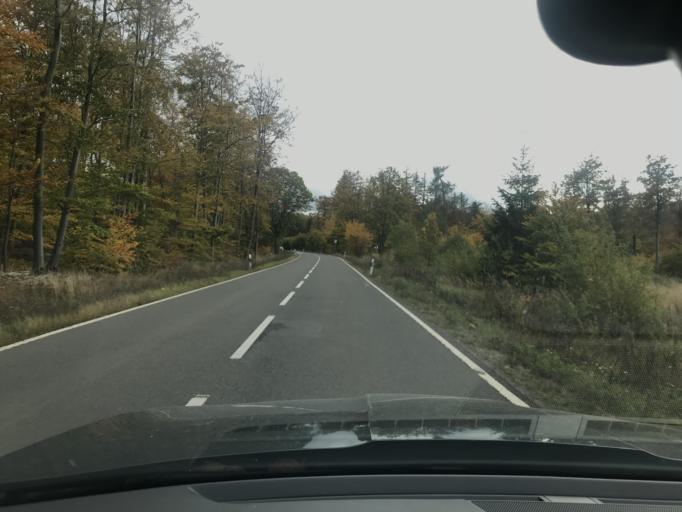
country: DE
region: Saxony-Anhalt
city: Friedrichsbrunn
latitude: 51.7045
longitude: 11.0238
